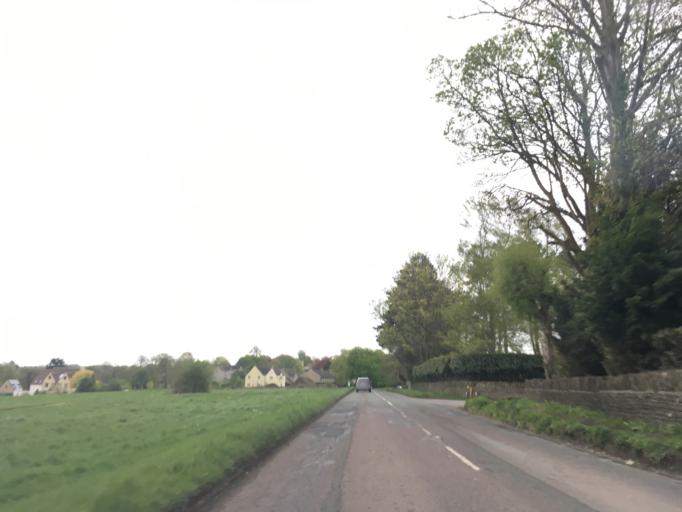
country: GB
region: England
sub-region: Gloucestershire
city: Stroud
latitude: 51.7258
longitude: -2.2142
